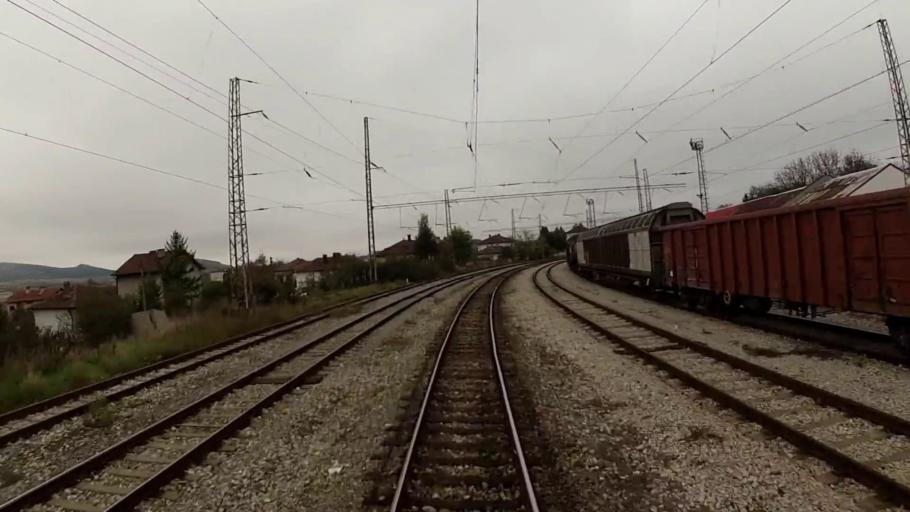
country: BG
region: Sofiya
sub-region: Obshtina Dragoman
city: Dragoman
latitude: 42.9293
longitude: 22.9322
